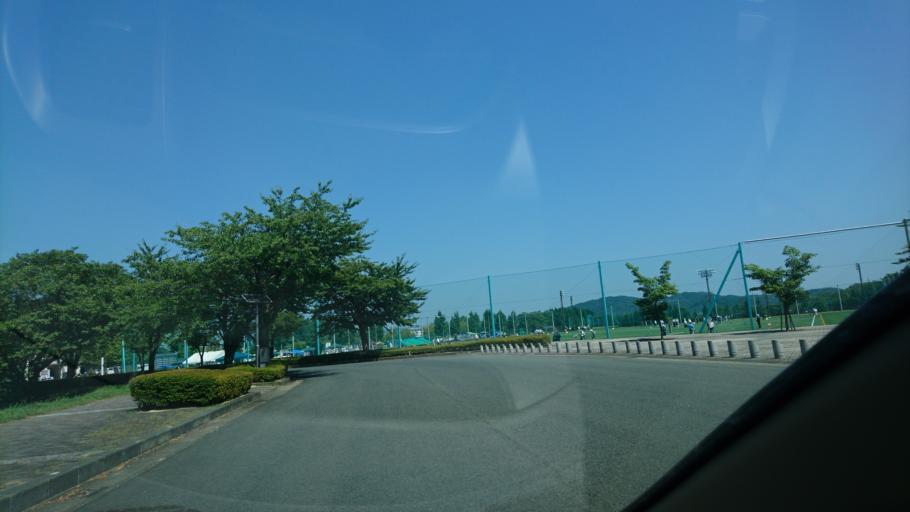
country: JP
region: Iwate
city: Kitakami
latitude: 39.2594
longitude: 141.0948
